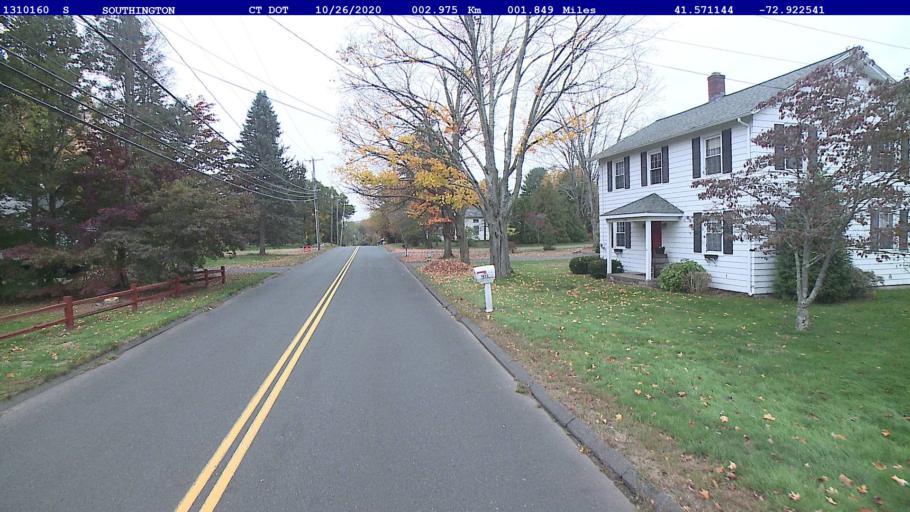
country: US
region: Connecticut
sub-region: New Haven County
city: Wolcott
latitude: 41.5711
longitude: -72.9225
